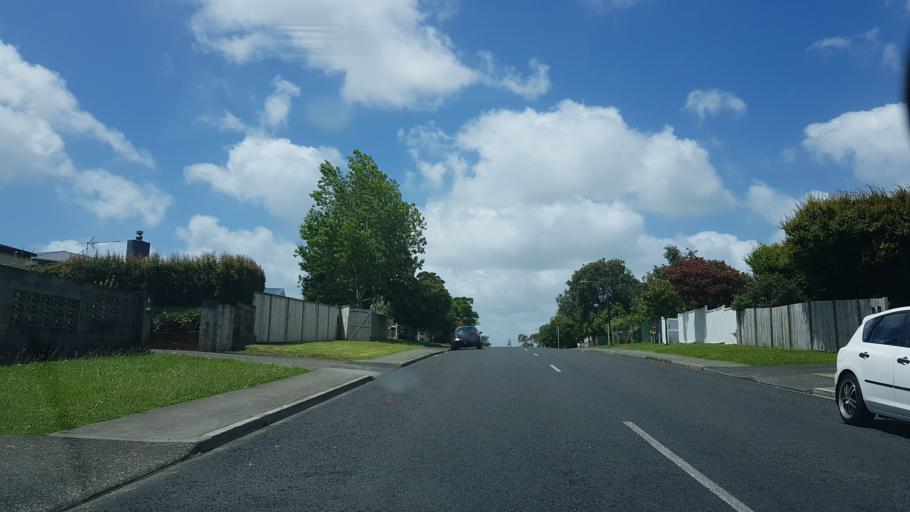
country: NZ
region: Auckland
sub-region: Auckland
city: North Shore
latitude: -36.7875
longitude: 174.7016
